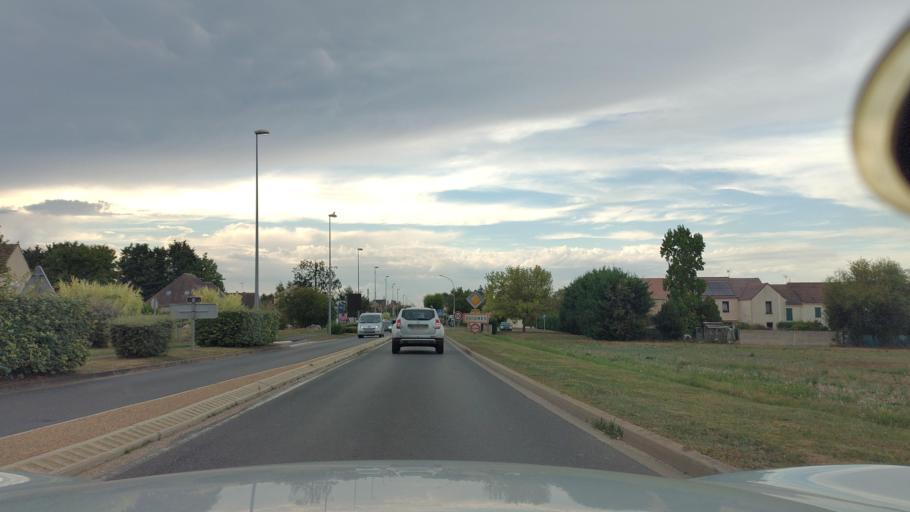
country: FR
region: Ile-de-France
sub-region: Departement de Seine-et-Marne
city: Guignes
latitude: 48.6314
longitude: 2.8089
